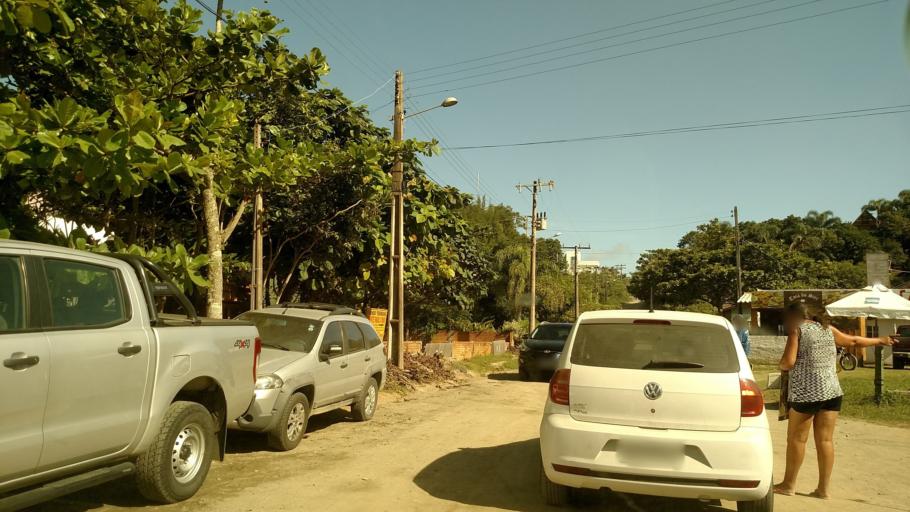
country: BR
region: Santa Catarina
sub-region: Porto Belo
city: Porto Belo
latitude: -27.2152
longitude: -48.5091
